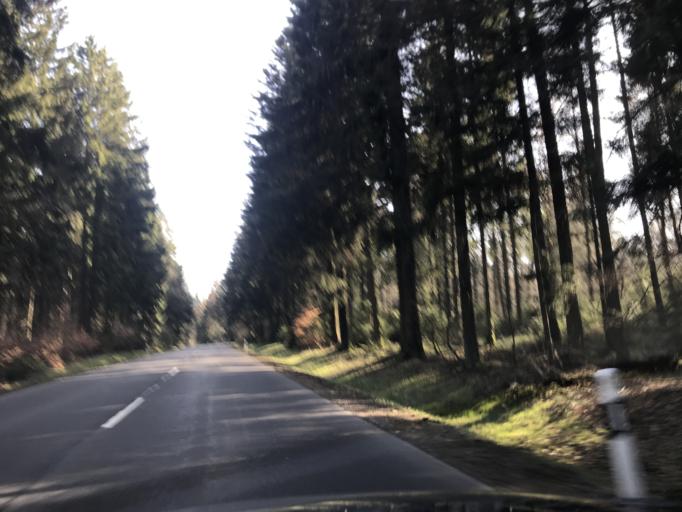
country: DE
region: Saarland
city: Nonnweiler
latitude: 49.6339
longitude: 6.9533
